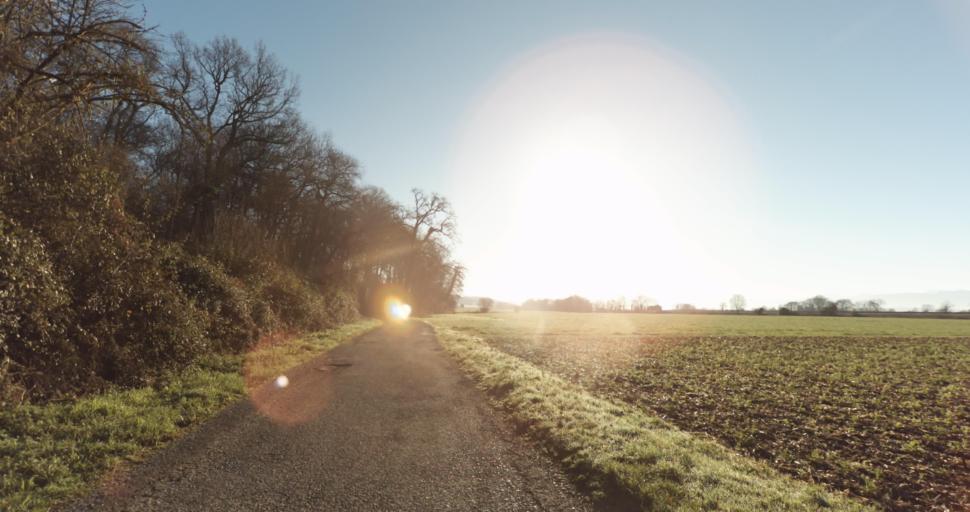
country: FR
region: Aquitaine
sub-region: Departement des Pyrenees-Atlantiques
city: Ousse
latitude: 43.3125
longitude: -0.2536
